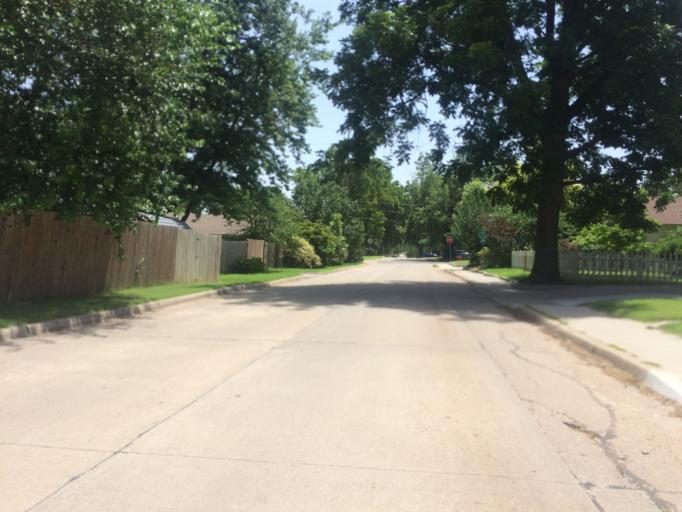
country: US
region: Oklahoma
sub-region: Cleveland County
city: Norman
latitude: 35.2155
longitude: -97.4547
